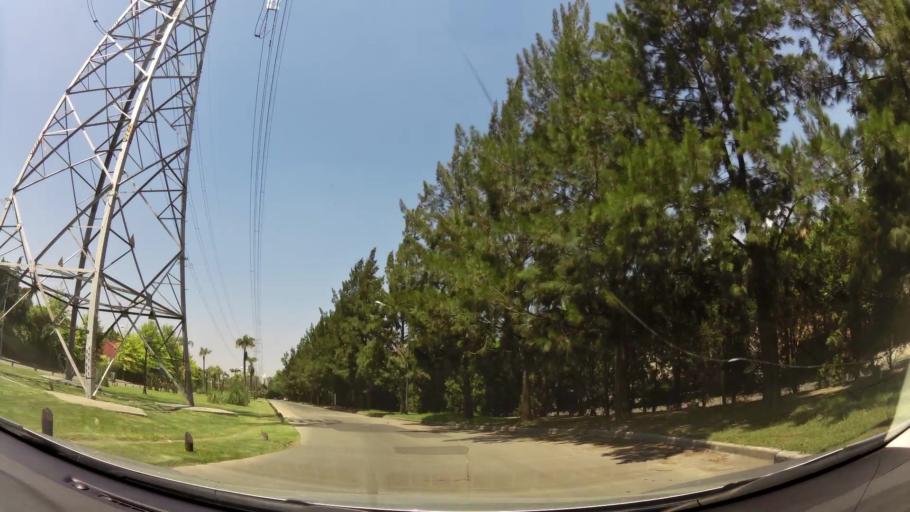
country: AR
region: Buenos Aires
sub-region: Partido de Tigre
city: Tigre
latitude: -34.4286
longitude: -58.6009
